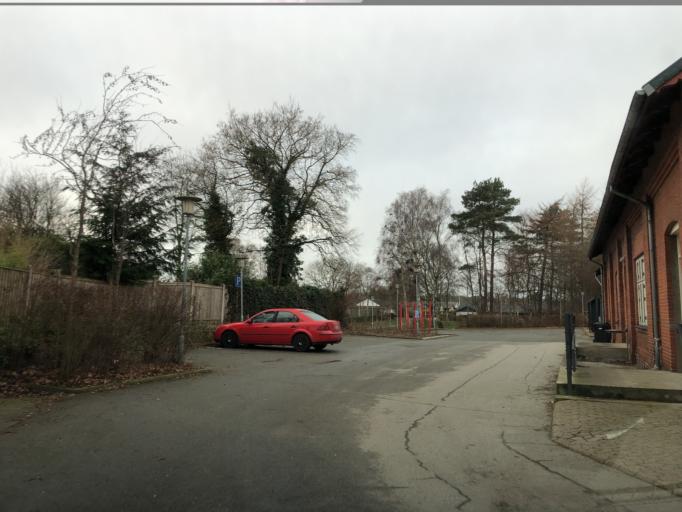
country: DK
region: Central Jutland
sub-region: Viborg Kommune
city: Stoholm
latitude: 56.4872
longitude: 9.1505
